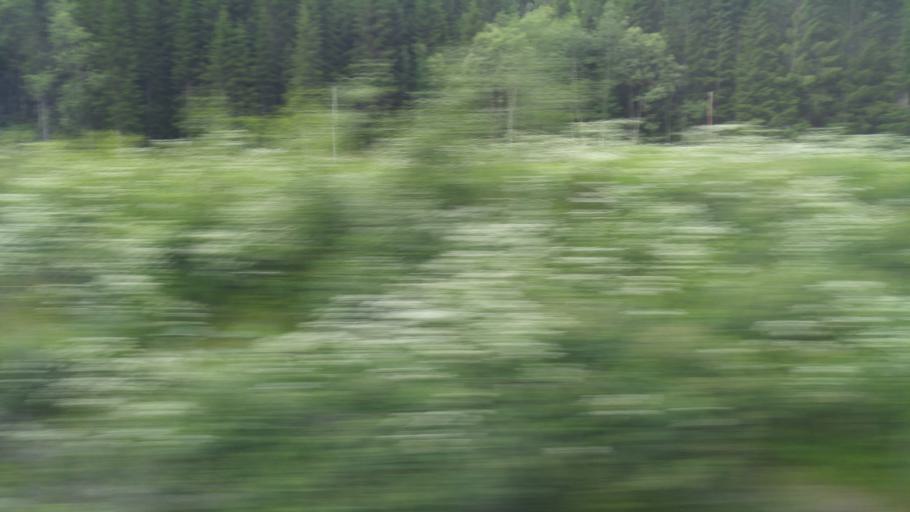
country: NO
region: Nord-Trondelag
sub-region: Levanger
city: Levanger
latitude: 63.4577
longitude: 11.3986
